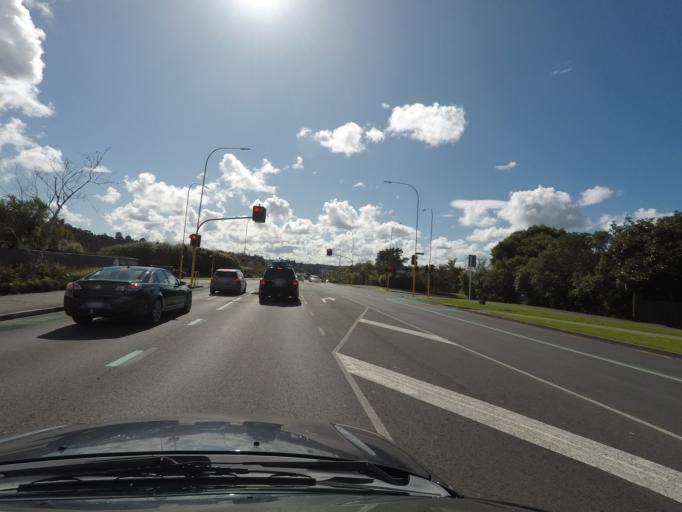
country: NZ
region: Auckland
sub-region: Auckland
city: Rothesay Bay
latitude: -36.7371
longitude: 174.6918
